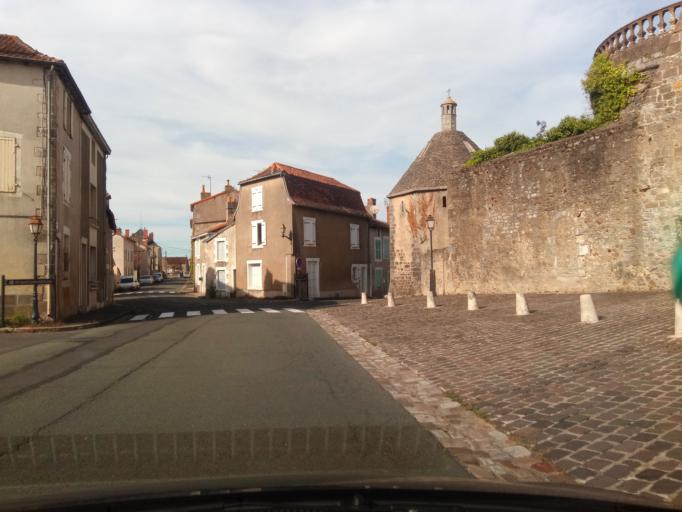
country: FR
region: Poitou-Charentes
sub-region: Departement de la Vienne
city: Montmorillon
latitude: 46.4226
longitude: 0.8635
